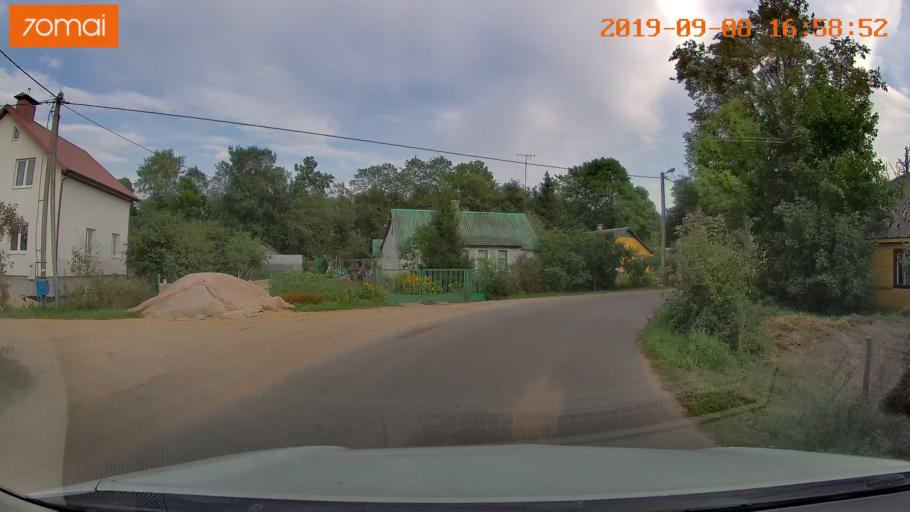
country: BY
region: Grodnenskaya
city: Hrodna
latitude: 53.7247
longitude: 23.9320
